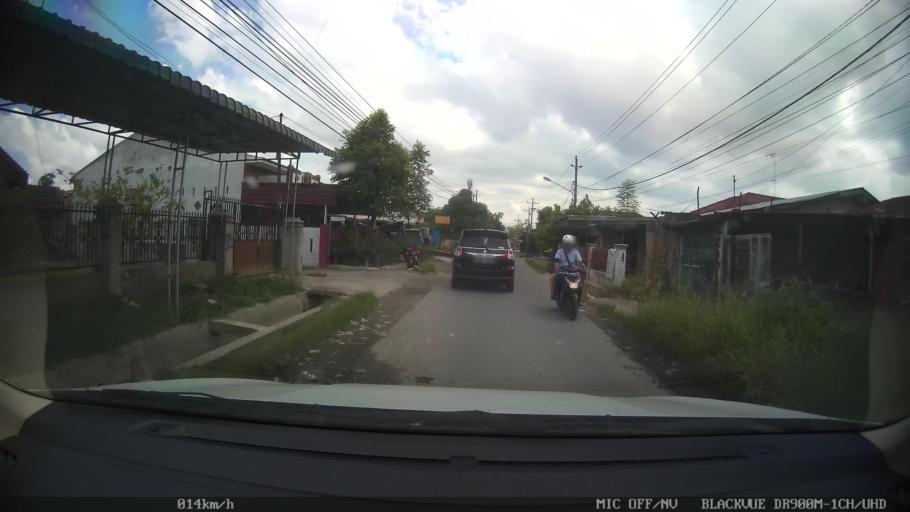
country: ID
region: North Sumatra
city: Sunggal
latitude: 3.6124
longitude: 98.6238
